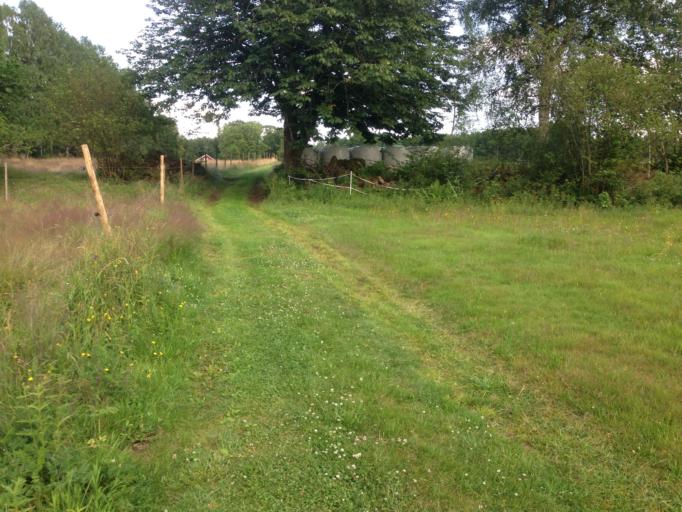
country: SE
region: Kronoberg
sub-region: Ljungby Kommun
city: Ljungby
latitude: 56.8685
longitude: 13.7800
